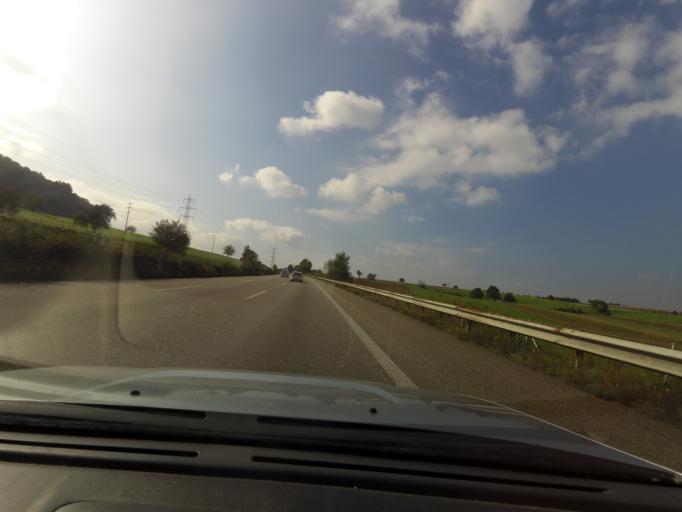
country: CH
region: Aargau
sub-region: Bezirk Rheinfelden
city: Mumpf
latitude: 47.5512
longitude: 7.8892
